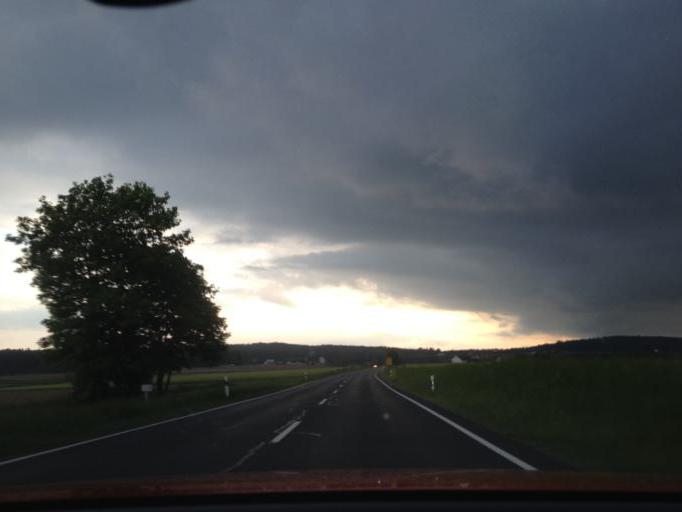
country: DE
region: Bavaria
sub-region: Upper Palatinate
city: Hahnbach
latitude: 49.5293
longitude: 11.7679
